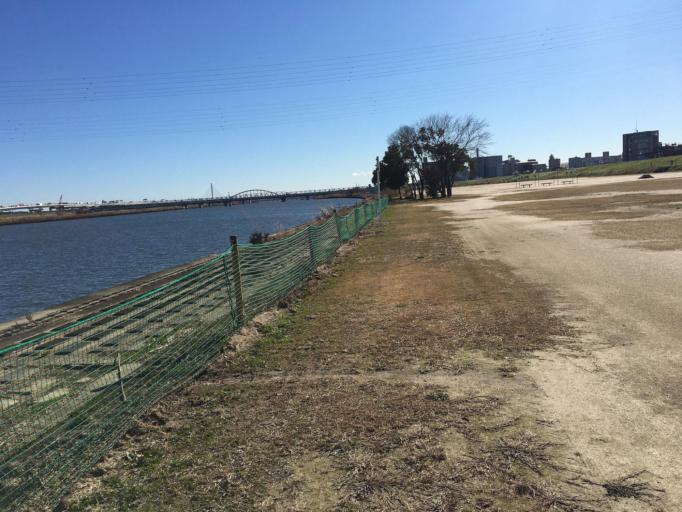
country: JP
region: Saitama
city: Soka
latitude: 35.7374
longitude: 139.8225
